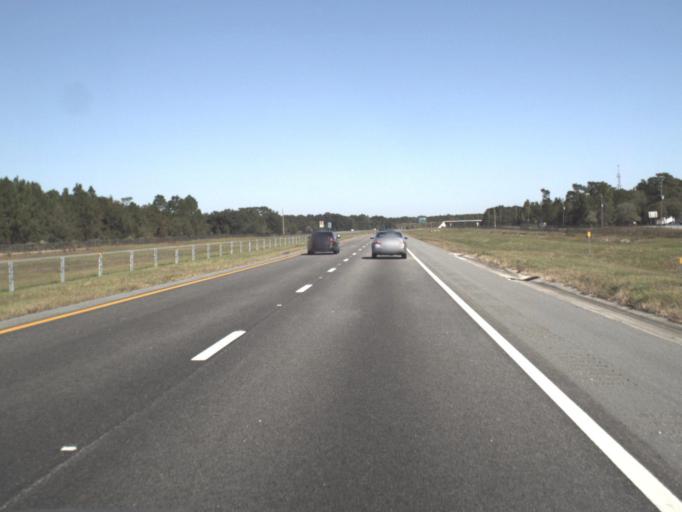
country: US
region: Florida
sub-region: Pasco County
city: Shady Hills
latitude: 28.3754
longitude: -82.5419
